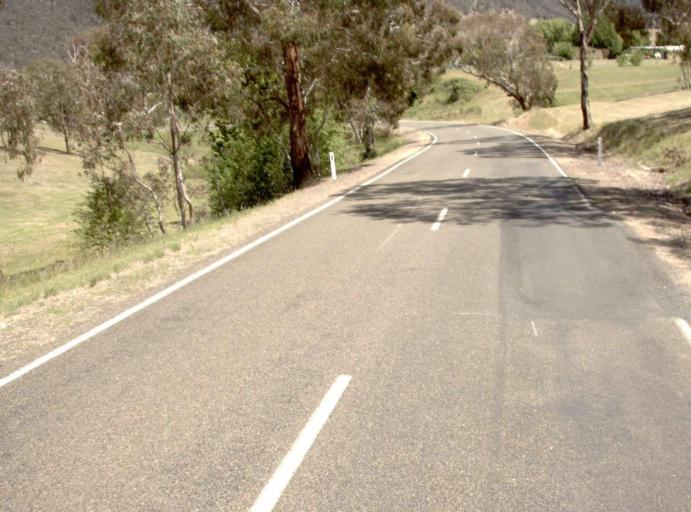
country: AU
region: Victoria
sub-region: Alpine
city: Mount Beauty
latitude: -37.0976
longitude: 147.5986
